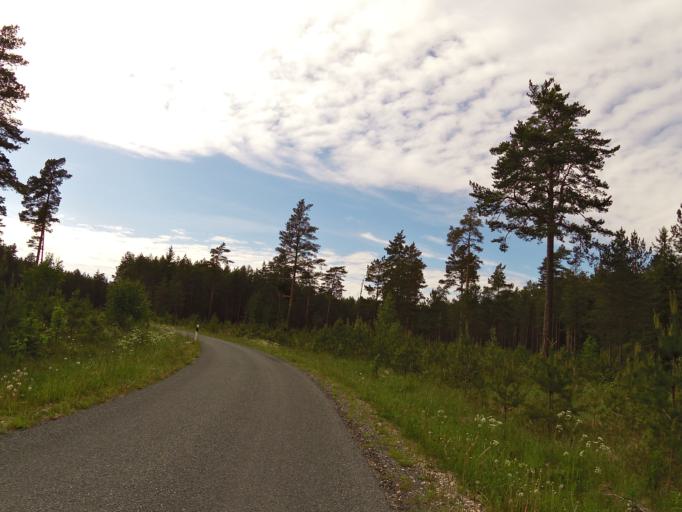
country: EE
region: Harju
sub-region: Paldiski linn
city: Paldiski
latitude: 59.2494
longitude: 23.7709
